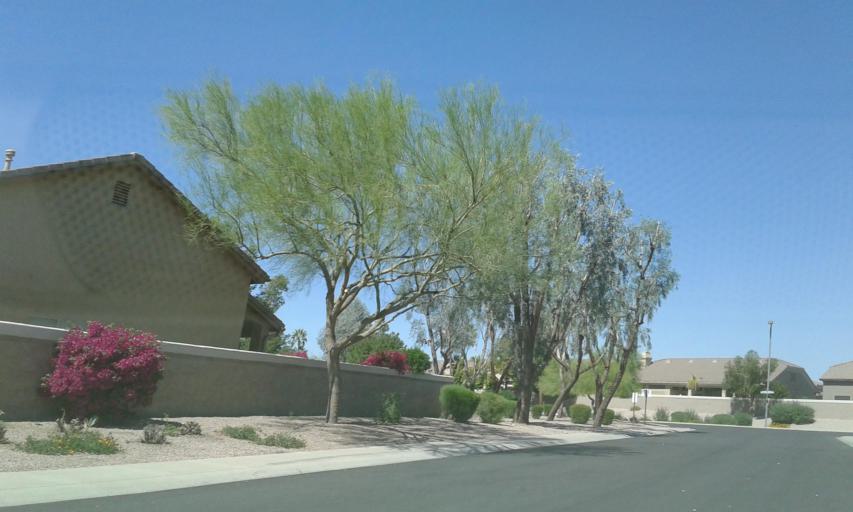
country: US
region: Arizona
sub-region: Maricopa County
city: Paradise Valley
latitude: 33.6515
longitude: -111.9712
